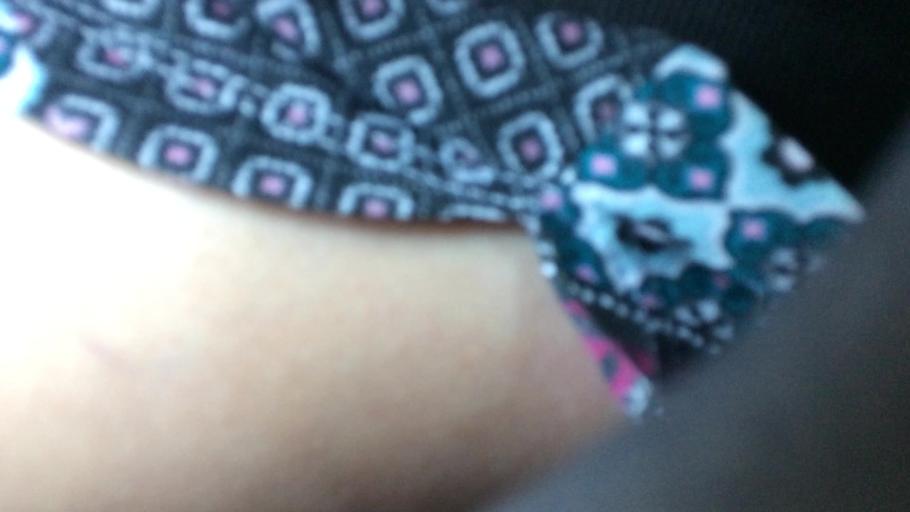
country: US
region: New Mexico
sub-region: San Miguel County
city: Las Vegas
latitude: 35.8473
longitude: -104.9350
